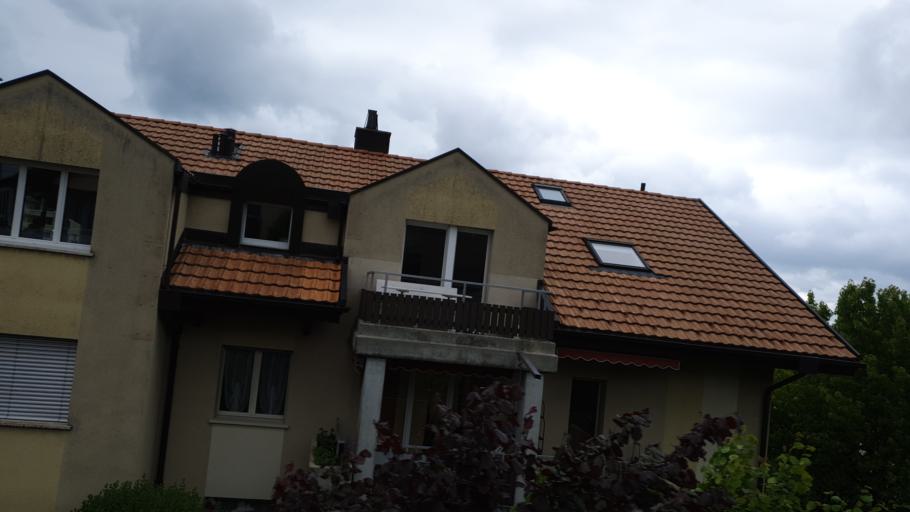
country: CH
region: Saint Gallen
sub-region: Wahlkreis Rorschach
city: Rorschach
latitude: 47.4756
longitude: 9.5214
